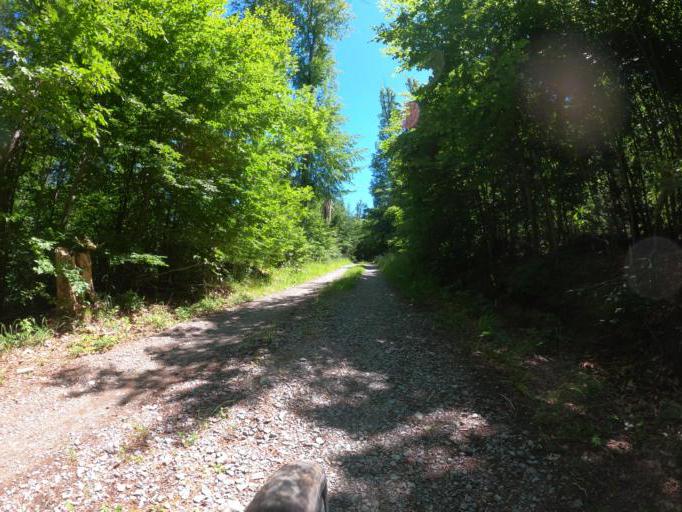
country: DE
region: Baden-Wuerttemberg
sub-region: Regierungsbezirk Stuttgart
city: Sersheim
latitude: 49.0061
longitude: 8.9841
